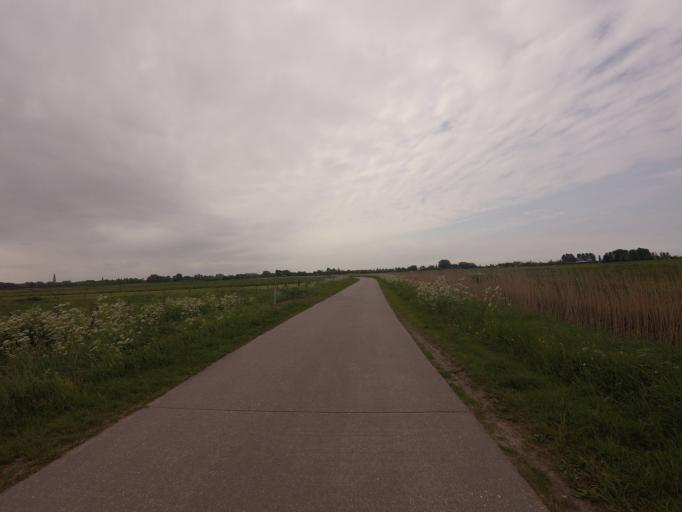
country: NL
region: Zeeland
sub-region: Gemeente Middelburg
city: Middelburg
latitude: 51.5151
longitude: 3.5892
